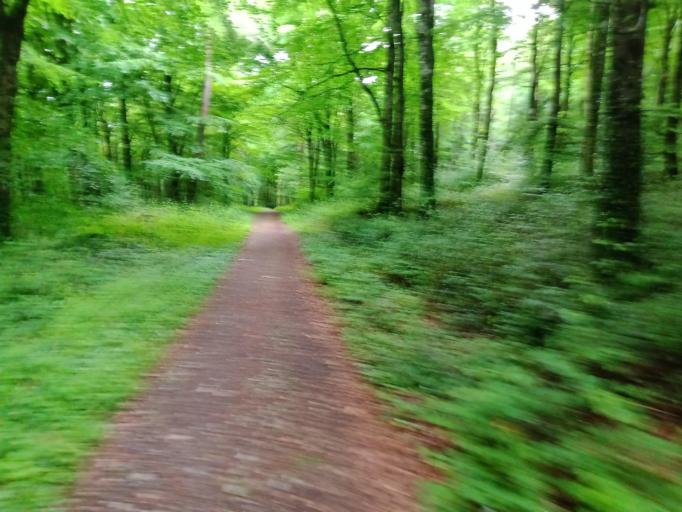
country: IE
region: Leinster
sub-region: Laois
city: Stradbally
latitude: 53.0010
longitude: -7.1221
